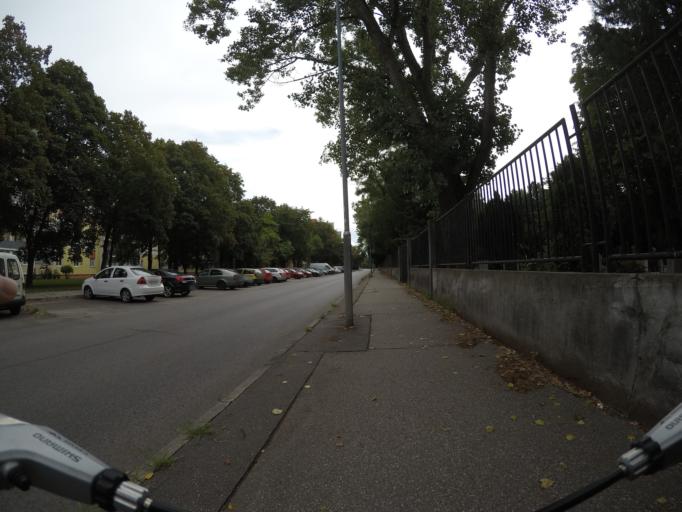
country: SK
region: Bratislavsky
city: Bratislava
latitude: 48.1633
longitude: 17.1623
